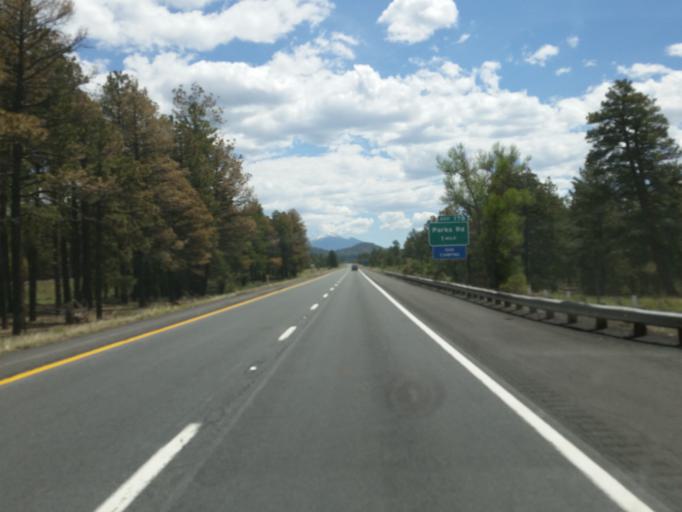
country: US
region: Arizona
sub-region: Coconino County
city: Parks
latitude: 35.2502
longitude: -111.9597
